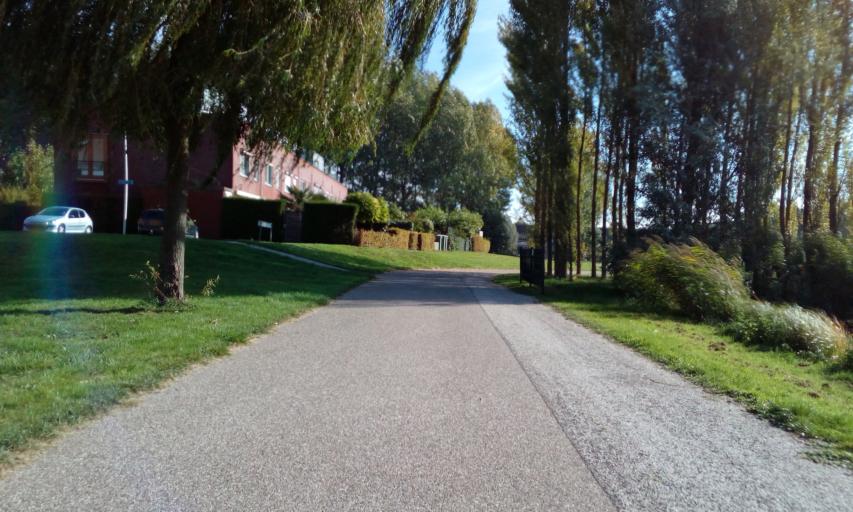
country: NL
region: Utrecht
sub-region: Gemeente IJsselstein
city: IJsselstein
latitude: 52.0769
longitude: 5.0229
